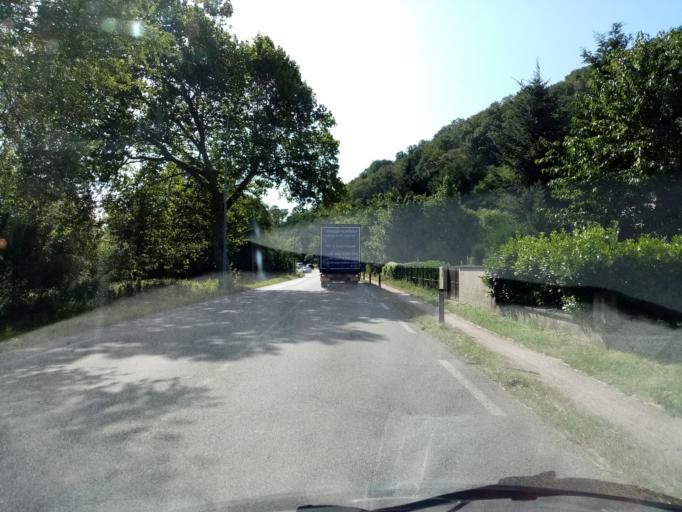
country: FR
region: Alsace
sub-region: Departement du Bas-Rhin
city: Chatenois
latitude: 48.2795
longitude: 7.3906
